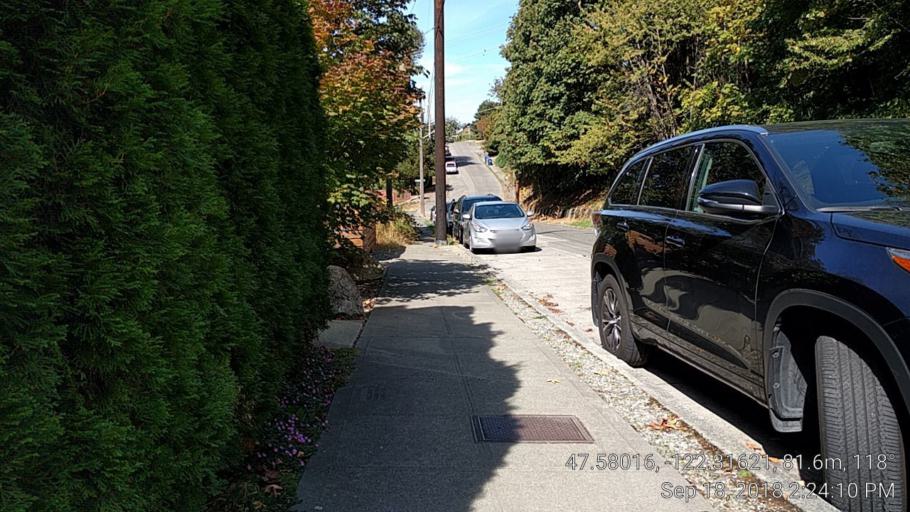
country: US
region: Washington
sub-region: King County
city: Seattle
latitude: 47.5802
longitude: -122.3162
